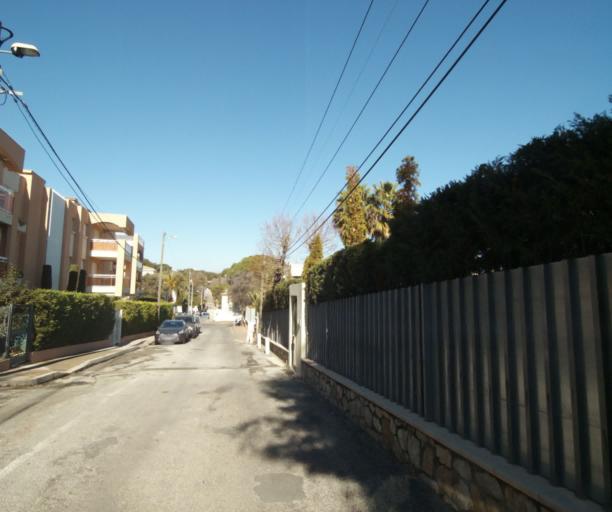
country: FR
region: Provence-Alpes-Cote d'Azur
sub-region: Departement des Alpes-Maritimes
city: Antibes
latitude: 43.5689
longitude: 7.1220
